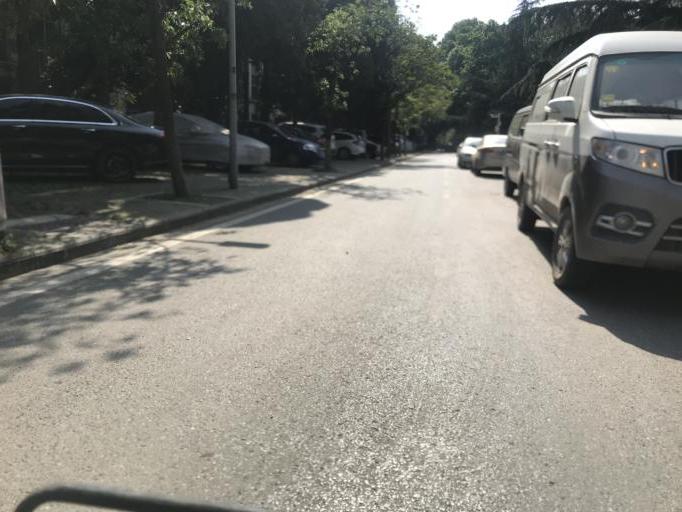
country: CN
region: Hubei
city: Guanshan
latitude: 30.5291
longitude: 114.3573
